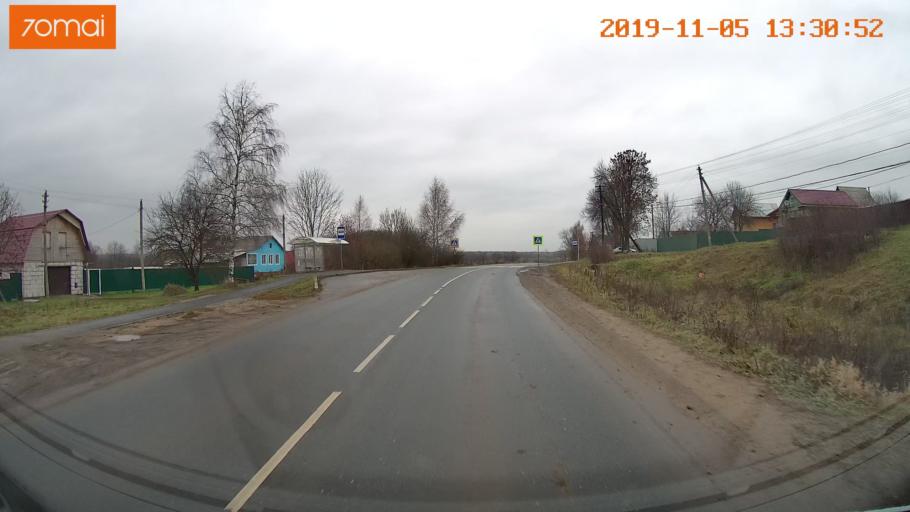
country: RU
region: Ivanovo
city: Shuya
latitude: 56.8700
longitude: 41.3937
